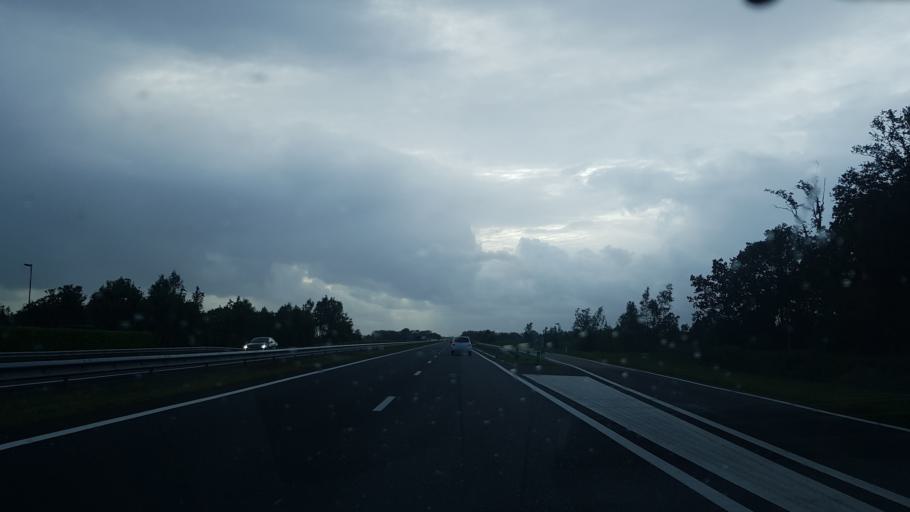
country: NL
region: Friesland
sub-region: Gemeente Tytsjerksteradiel
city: Garyp
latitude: 53.1541
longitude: 5.9705
